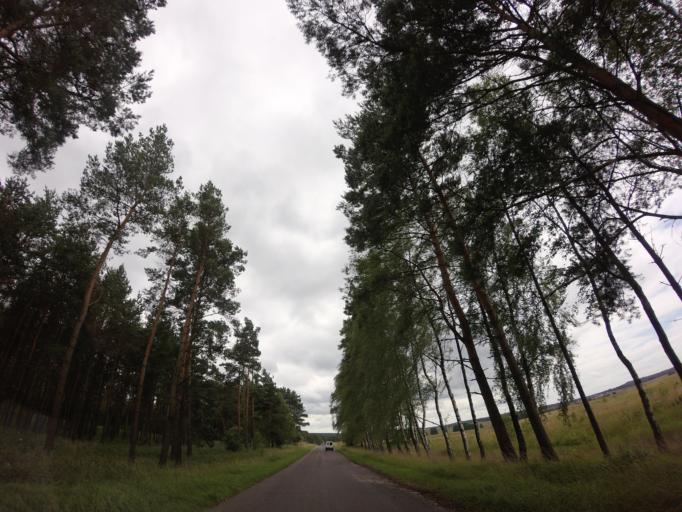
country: PL
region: West Pomeranian Voivodeship
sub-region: Powiat stargardzki
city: Insko
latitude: 53.4139
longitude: 15.6021
